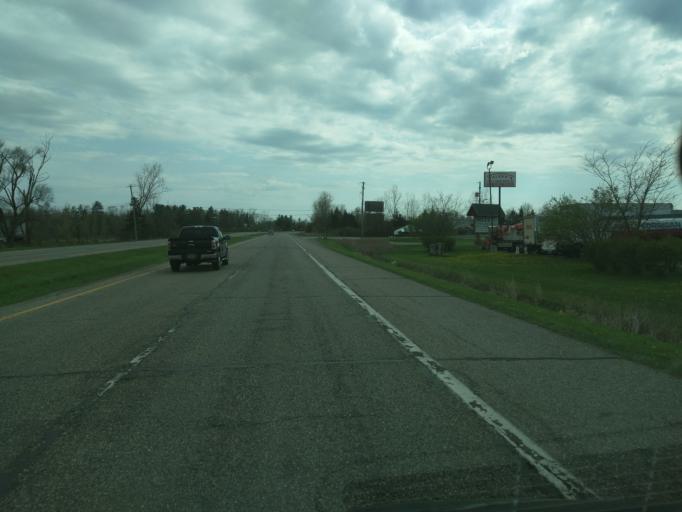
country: US
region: Michigan
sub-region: Eaton County
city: Dimondale
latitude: 42.6916
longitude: -84.6359
